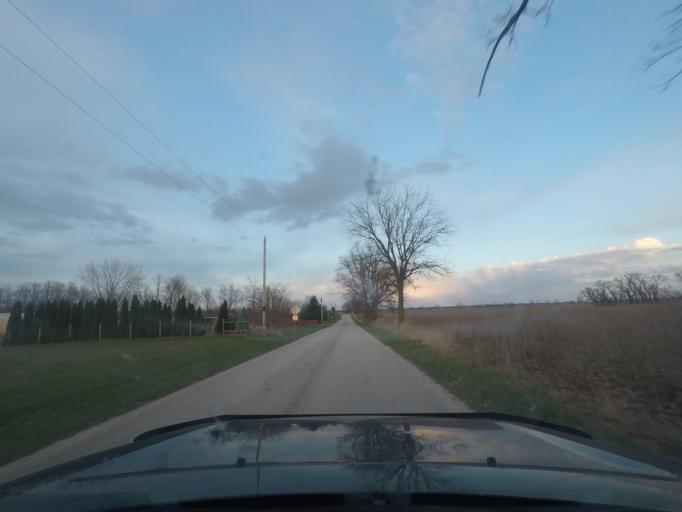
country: US
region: Indiana
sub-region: LaPorte County
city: Kingsford Heights
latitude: 41.4665
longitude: -86.7035
